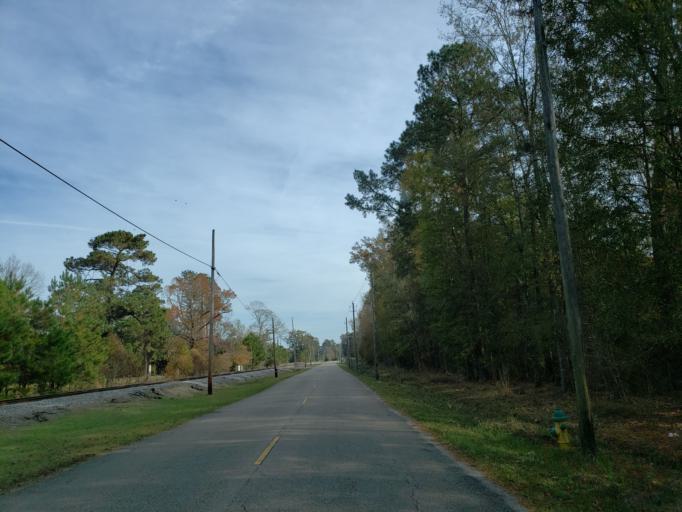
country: US
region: Mississippi
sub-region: Forrest County
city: Glendale
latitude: 31.3523
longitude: -89.3260
